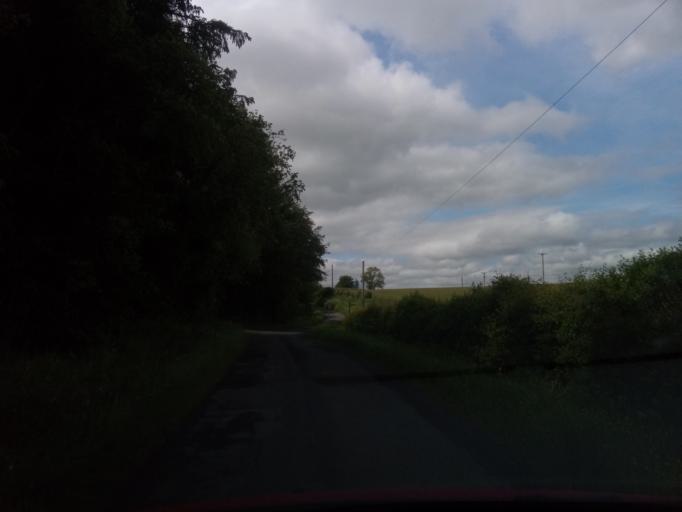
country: GB
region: Scotland
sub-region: The Scottish Borders
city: Selkirk
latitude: 55.5305
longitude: -2.8501
